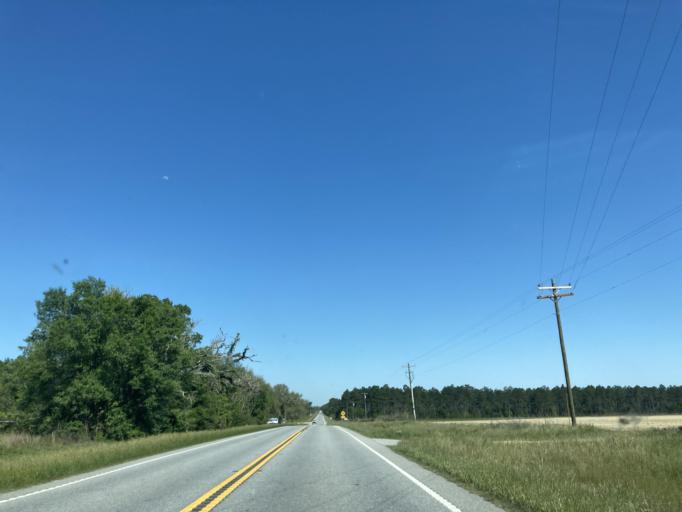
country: US
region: Georgia
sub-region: Miller County
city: Colquitt
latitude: 31.1844
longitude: -84.5739
